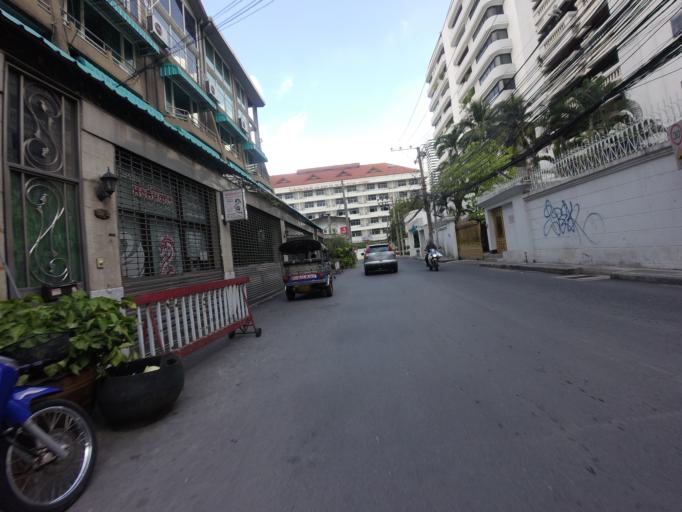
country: TH
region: Bangkok
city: Din Daeng
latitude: 13.7443
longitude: 100.5581
